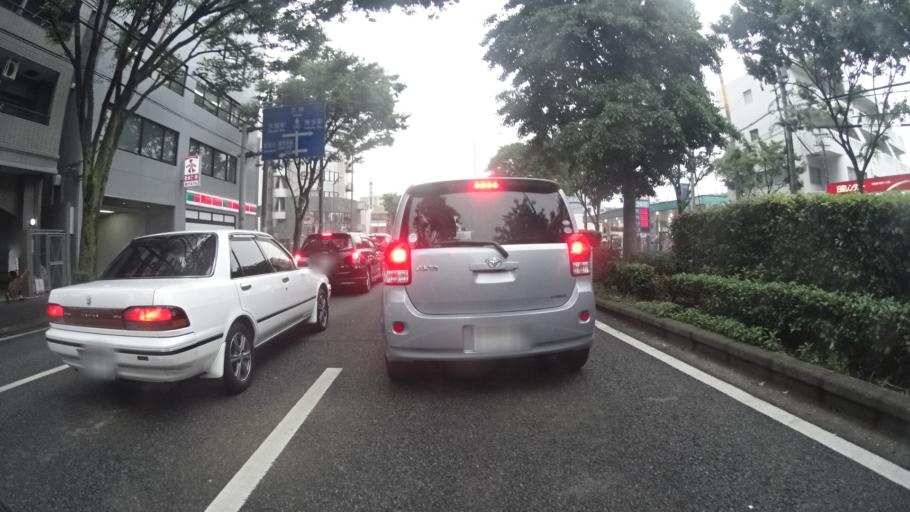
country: JP
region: Fukuoka
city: Fukuoka-shi
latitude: 33.5589
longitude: 130.4293
